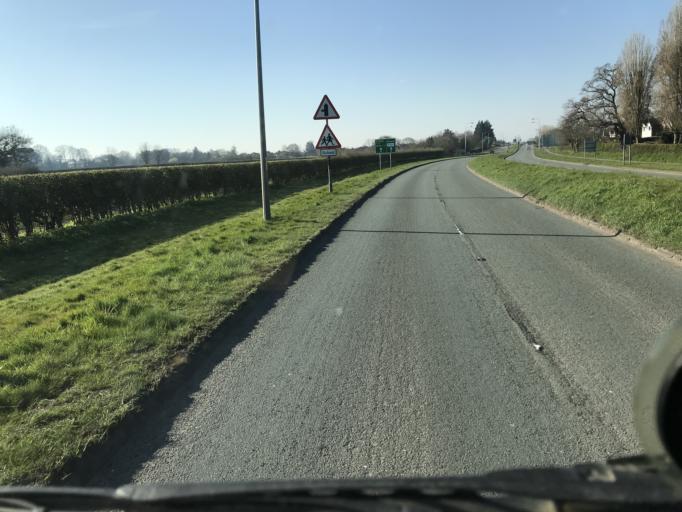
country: GB
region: England
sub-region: Cheshire West and Chester
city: Guilden Sutton
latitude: 53.1930
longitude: -2.8484
